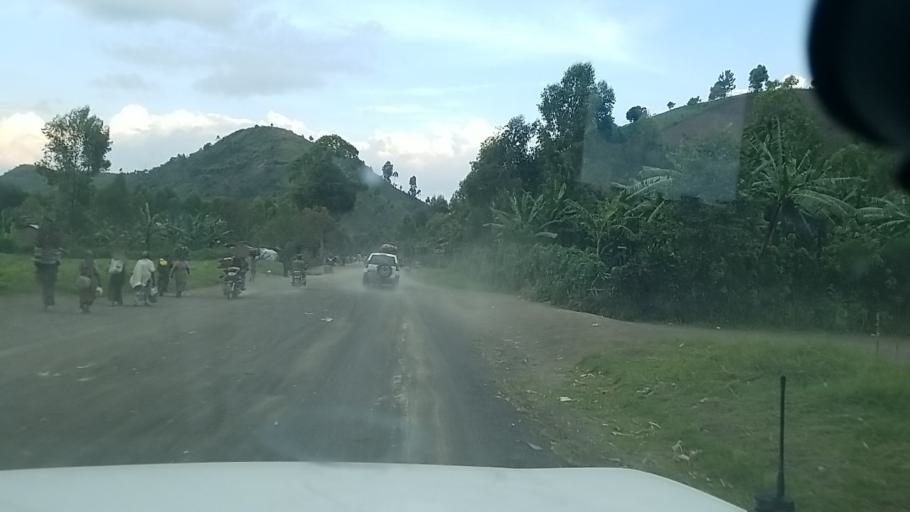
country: CD
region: Nord Kivu
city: Sake
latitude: -1.5689
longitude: 29.0446
